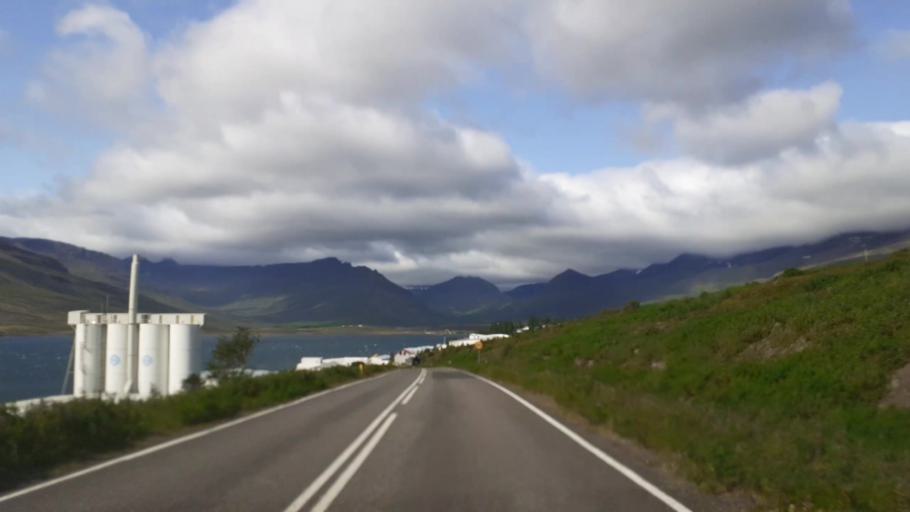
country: IS
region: East
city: Eskifjoerdur
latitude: 64.9247
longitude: -13.9866
